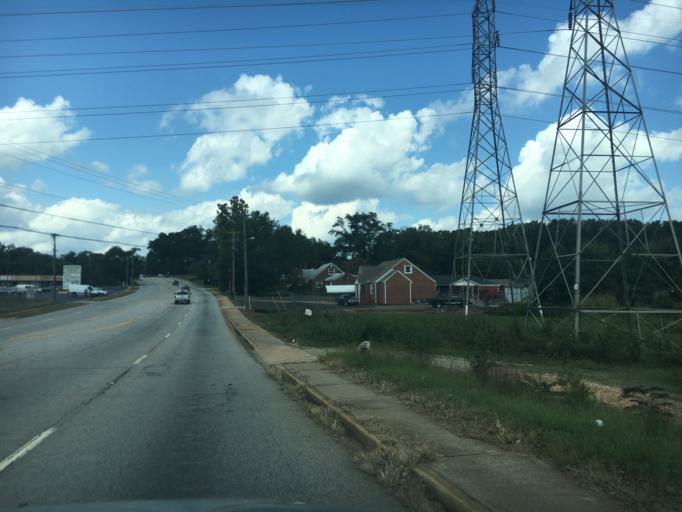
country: US
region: South Carolina
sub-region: Greenville County
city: Berea
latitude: 34.8792
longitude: -82.4469
